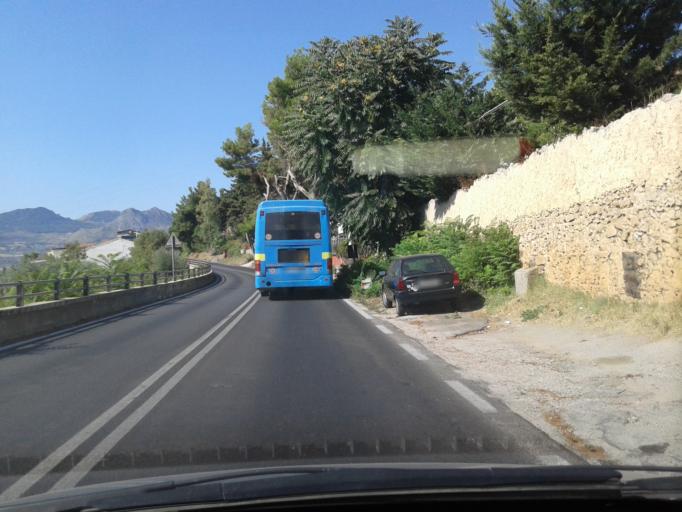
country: IT
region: Sicily
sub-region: Palermo
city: Cannizzaro-Favara
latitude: 38.0661
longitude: 13.2680
